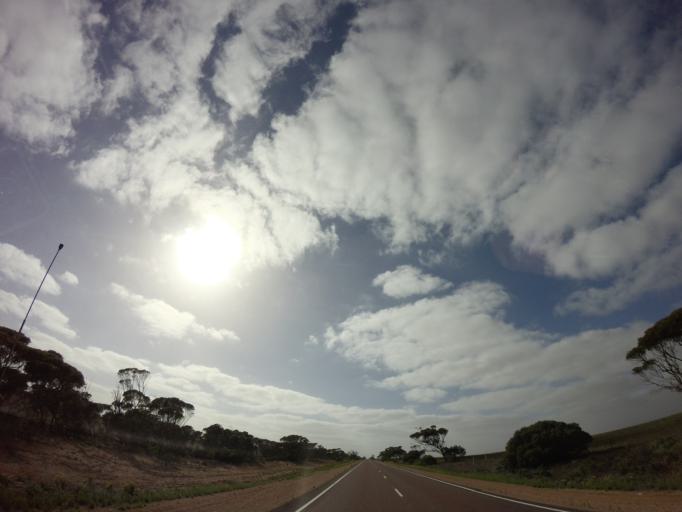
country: AU
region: South Australia
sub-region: Streaky Bay
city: Streaky Bay
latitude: -32.2846
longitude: 134.2285
